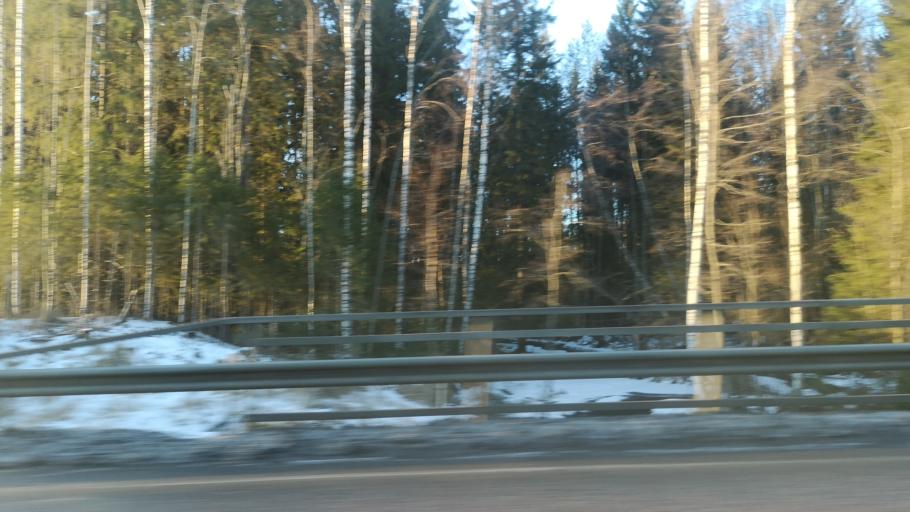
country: FI
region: Southern Savonia
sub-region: Pieksaemaeki
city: Juva
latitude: 61.8905
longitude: 27.7971
